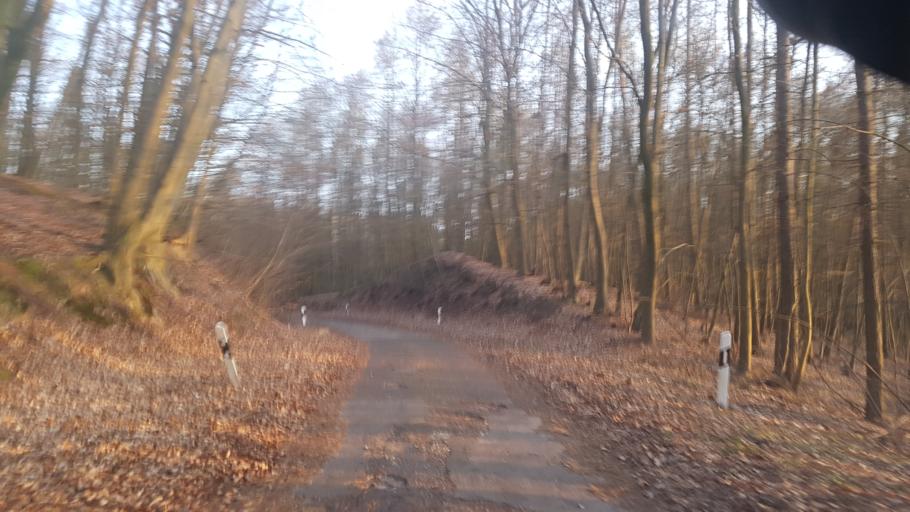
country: DE
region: Brandenburg
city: Gramzow
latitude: 53.2003
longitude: 13.9350
